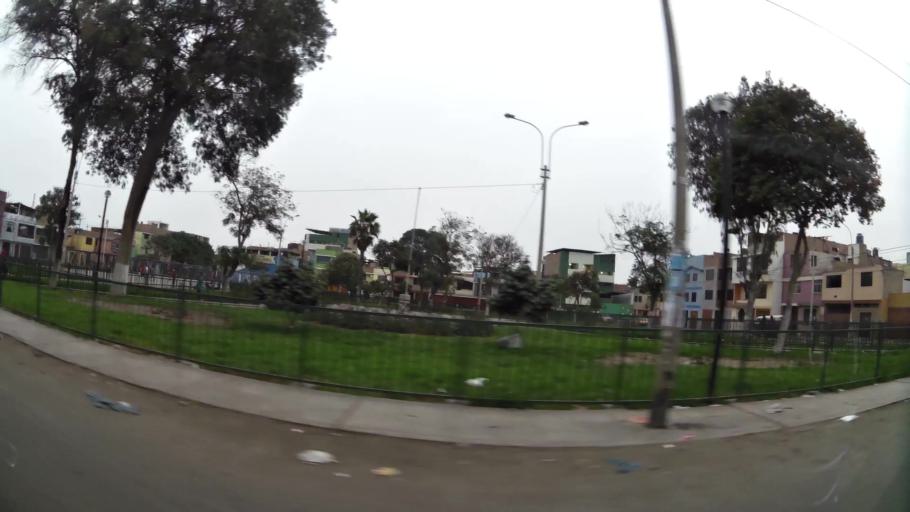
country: PE
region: Lima
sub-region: Lima
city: Surco
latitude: -12.1673
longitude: -76.9757
